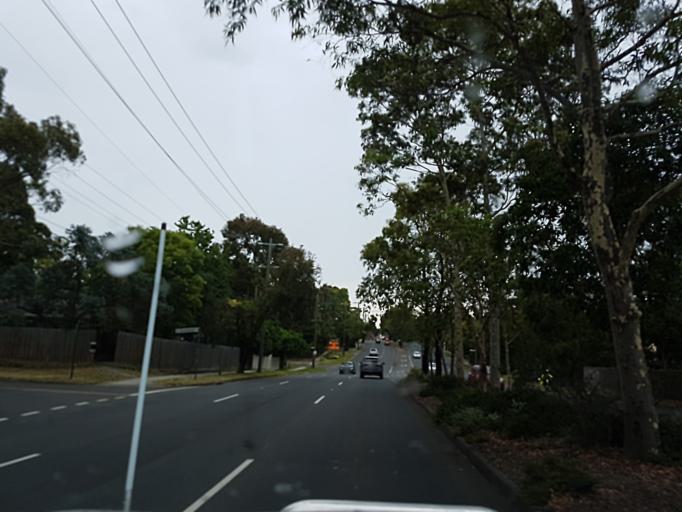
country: AU
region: Victoria
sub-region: Whitehorse
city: Forest Hill
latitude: -37.8333
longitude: 145.1607
